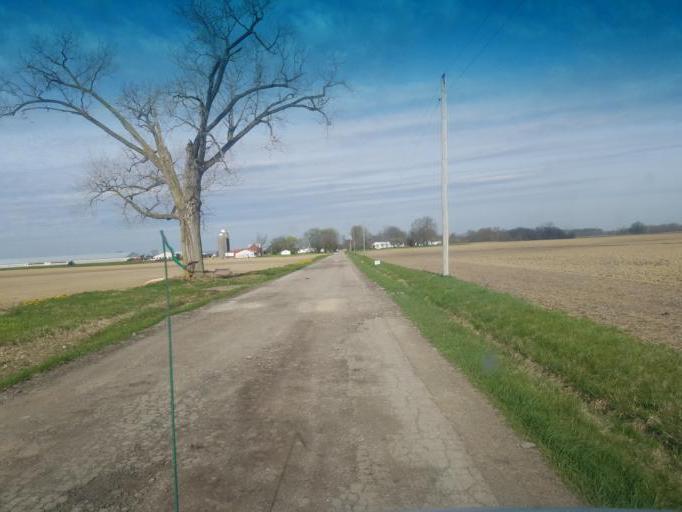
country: US
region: Ohio
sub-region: Delaware County
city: Ashley
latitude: 40.4387
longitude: -82.9528
